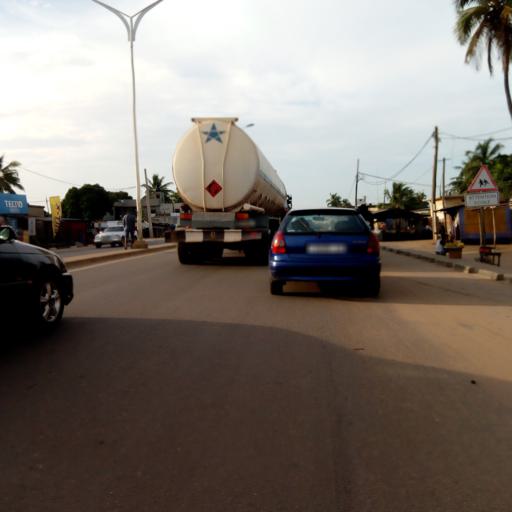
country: TG
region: Maritime
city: Lome
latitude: 6.1652
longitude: 1.2835
